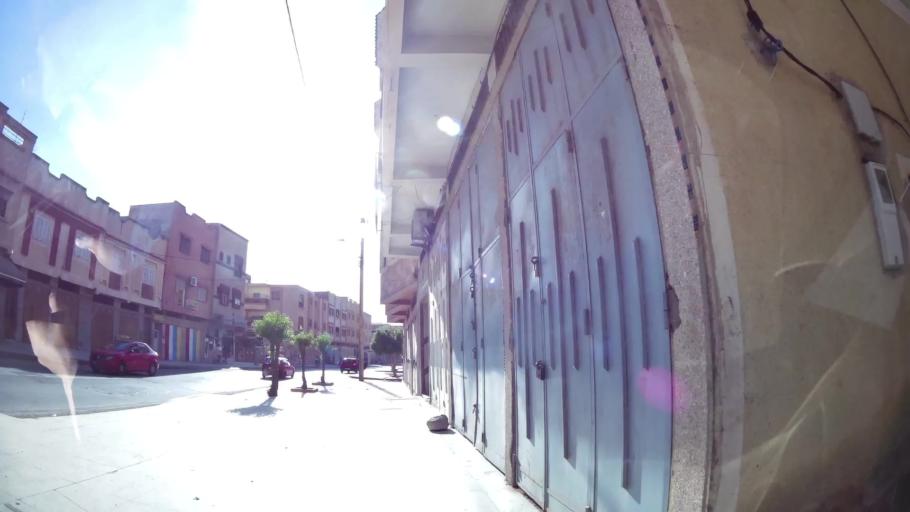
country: MA
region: Oriental
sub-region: Oujda-Angad
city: Oujda
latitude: 34.6706
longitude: -1.8975
